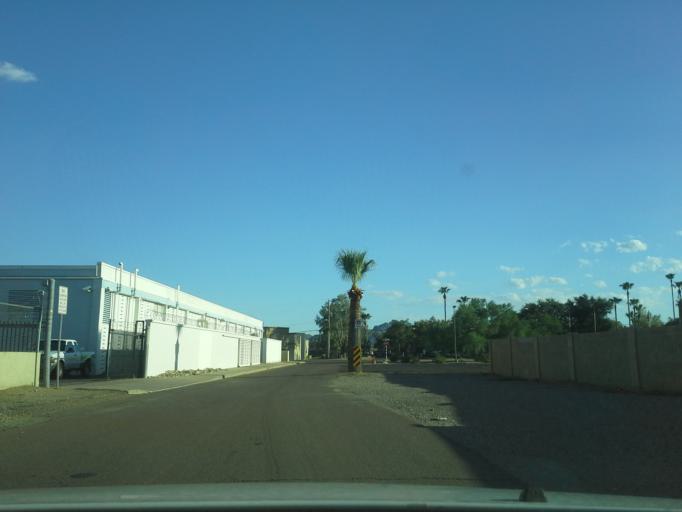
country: US
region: Arizona
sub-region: Maricopa County
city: Paradise Valley
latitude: 33.6128
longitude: -112.0155
